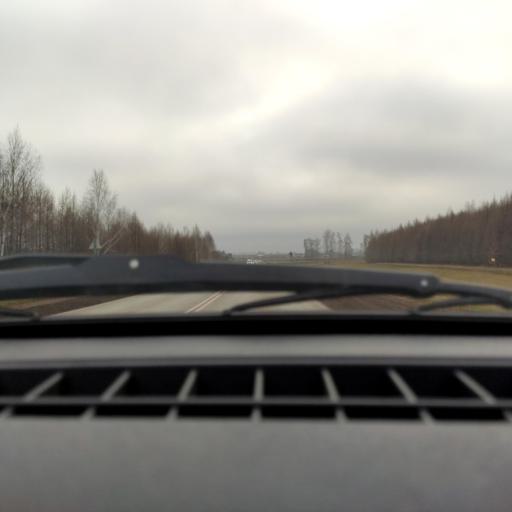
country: RU
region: Bashkortostan
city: Chishmy
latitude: 54.5775
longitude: 55.3622
